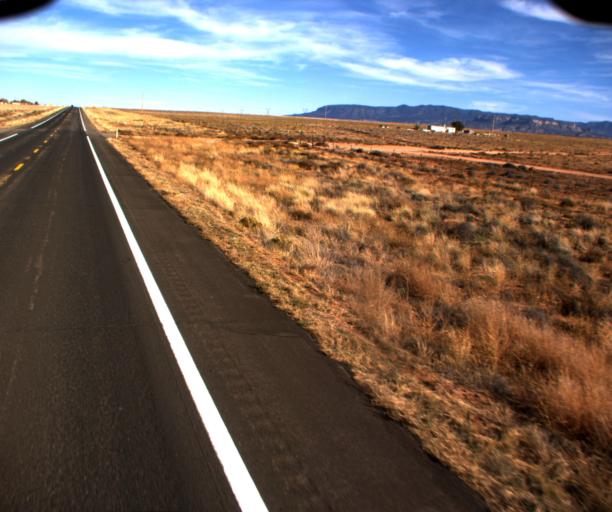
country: US
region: Arizona
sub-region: Apache County
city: Lukachukai
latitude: 36.9613
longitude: -109.3959
